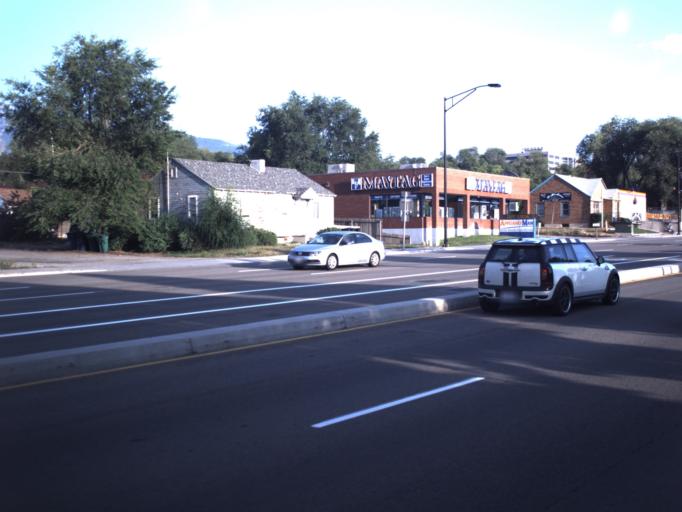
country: US
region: Utah
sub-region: Salt Lake County
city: Sandy City
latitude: 40.5872
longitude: -111.8910
